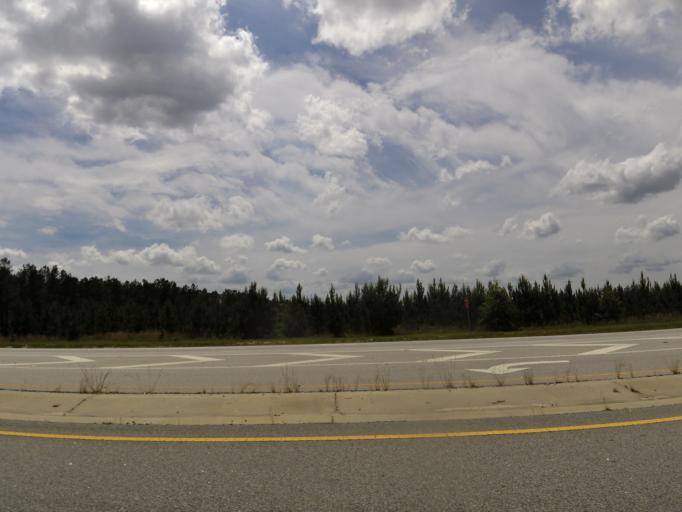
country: US
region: Georgia
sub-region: Emanuel County
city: Swainsboro
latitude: 32.7165
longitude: -82.3923
